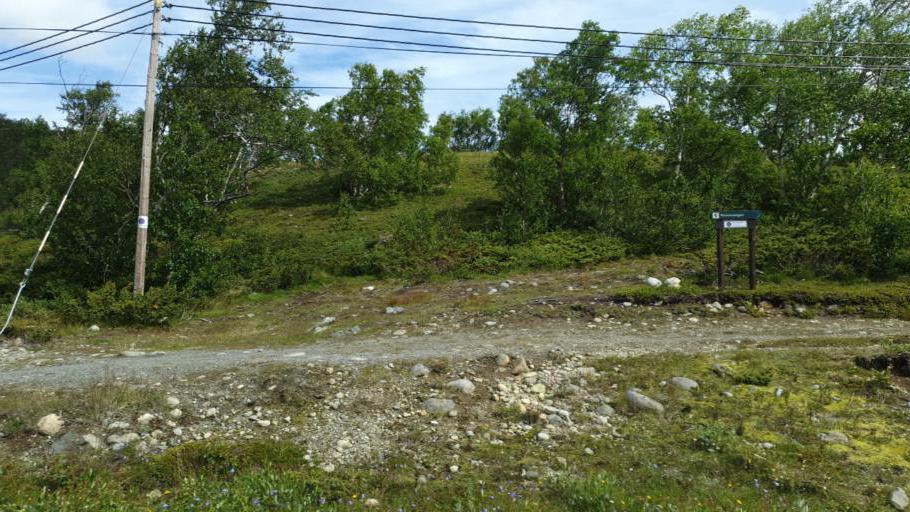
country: NO
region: Oppland
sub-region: Oystre Slidre
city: Heggenes
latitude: 61.4885
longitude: 8.8274
